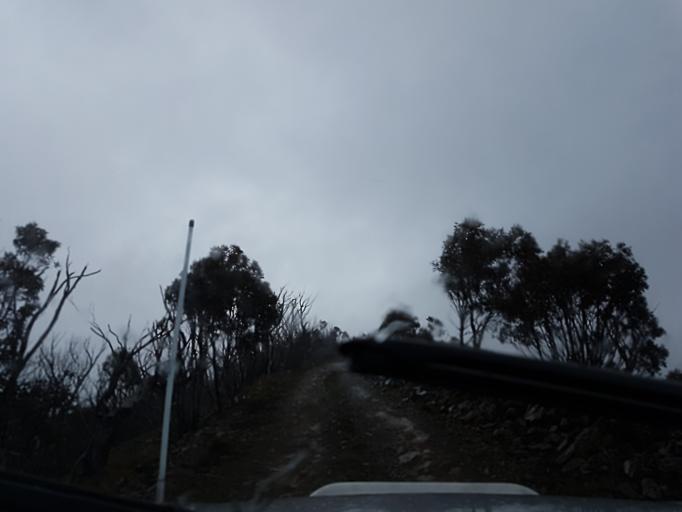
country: AU
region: Victoria
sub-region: Alpine
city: Mount Beauty
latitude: -37.0916
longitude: 147.0688
